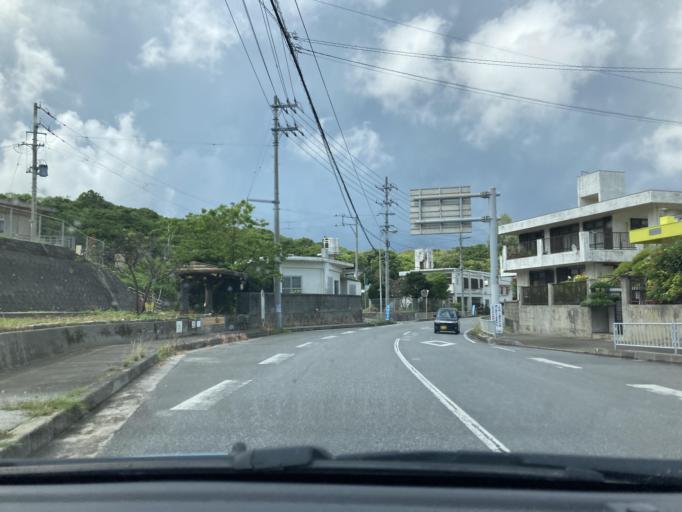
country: JP
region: Okinawa
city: Tomigusuku
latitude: 26.1772
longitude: 127.7451
